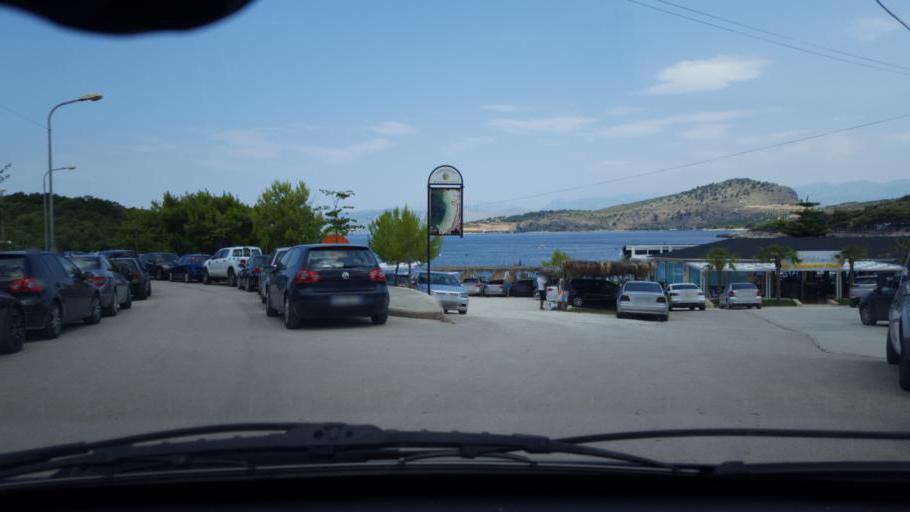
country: AL
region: Vlore
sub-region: Rrethi i Sarandes
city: Xarre
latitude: 39.7724
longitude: 19.9986
